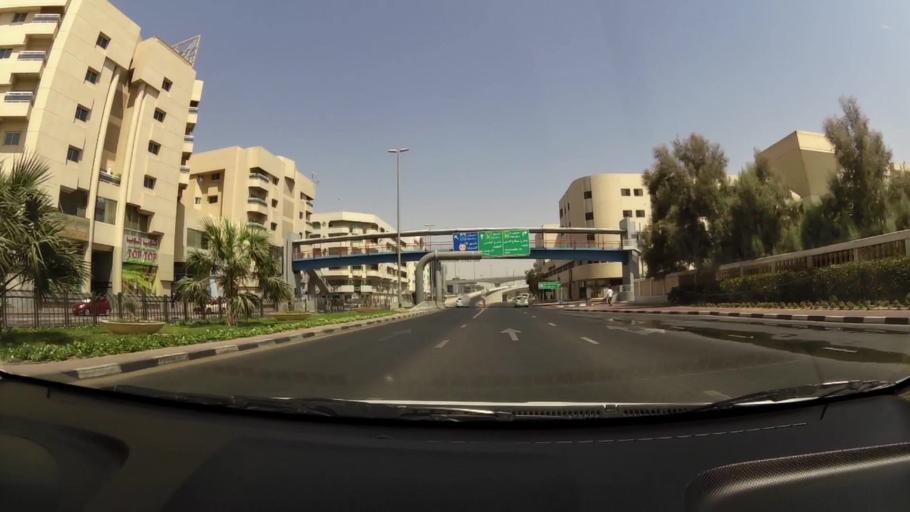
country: AE
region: Ash Shariqah
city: Sharjah
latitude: 25.2780
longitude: 55.3457
